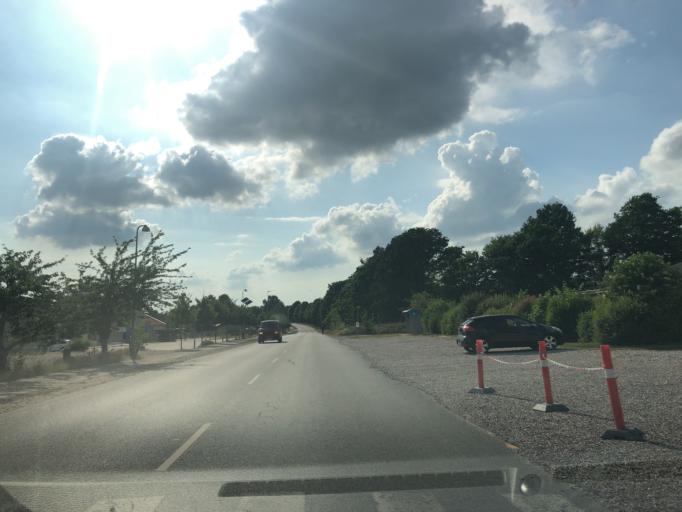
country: DK
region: Zealand
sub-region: Stevns Kommune
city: Store Heddinge
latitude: 55.2578
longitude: 12.3794
